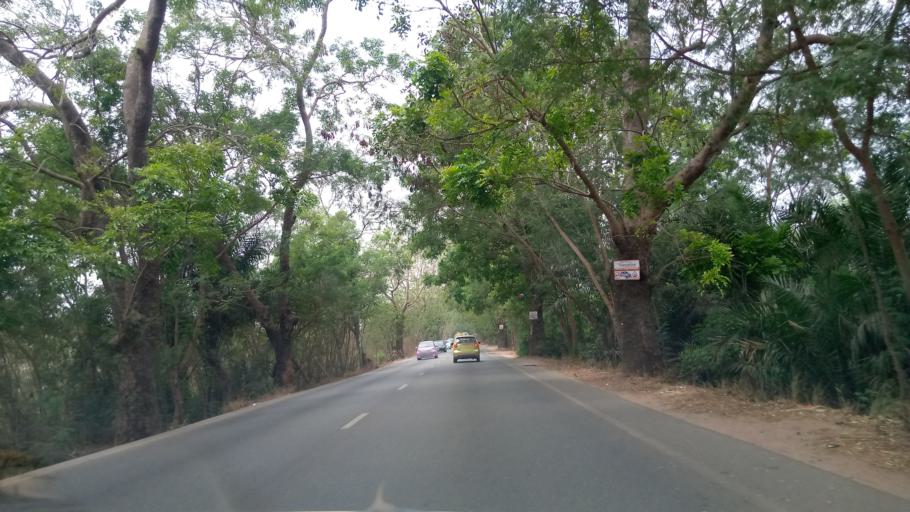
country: GH
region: Greater Accra
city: Dome
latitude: 5.6676
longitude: -0.2240
